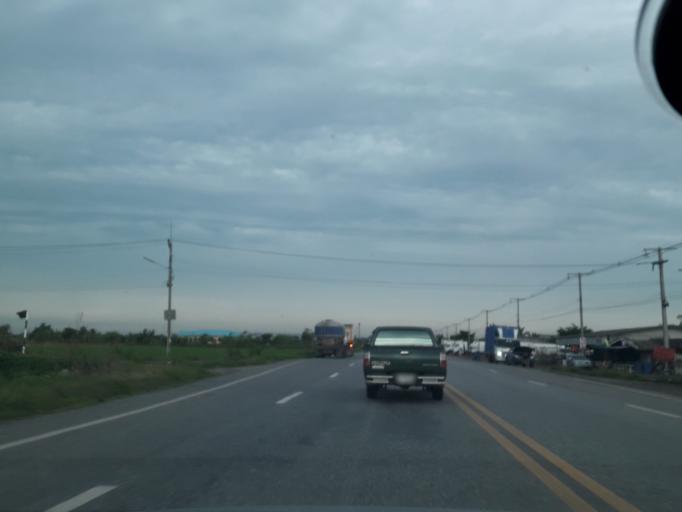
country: TH
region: Pathum Thani
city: Nong Suea
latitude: 14.1529
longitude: 100.7473
